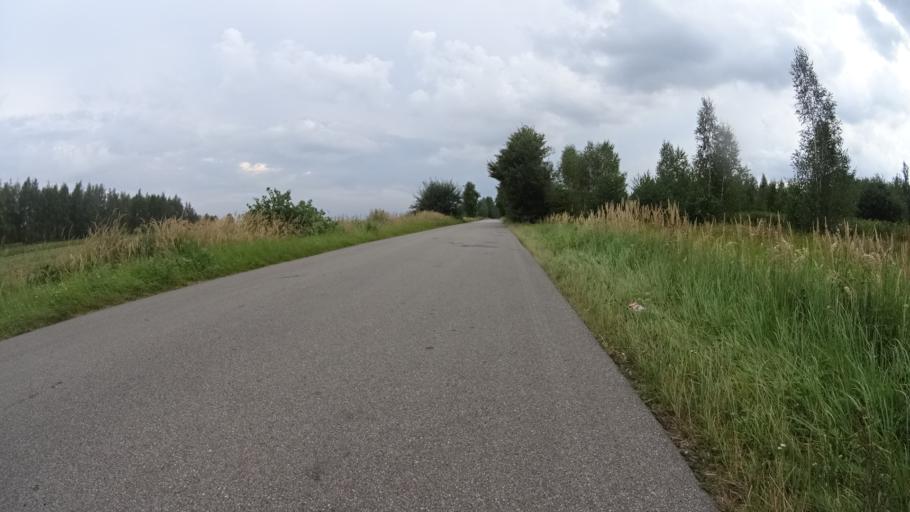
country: PL
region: Masovian Voivodeship
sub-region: Powiat grojecki
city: Goszczyn
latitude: 51.6821
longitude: 20.8606
